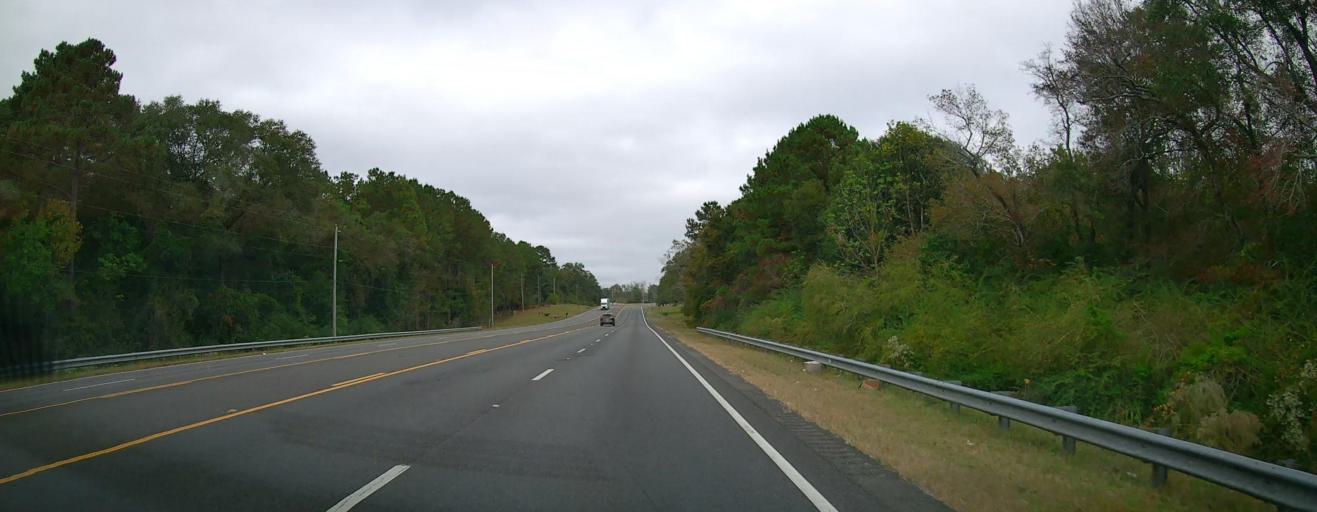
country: US
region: Georgia
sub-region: Thomas County
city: Thomasville
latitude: 30.9341
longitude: -83.9109
